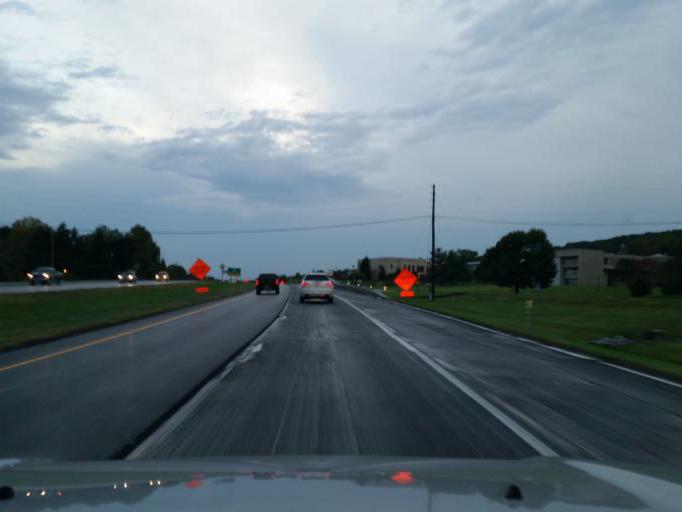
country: US
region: Maryland
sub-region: Frederick County
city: Emmitsburg
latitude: 39.6826
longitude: -77.3478
